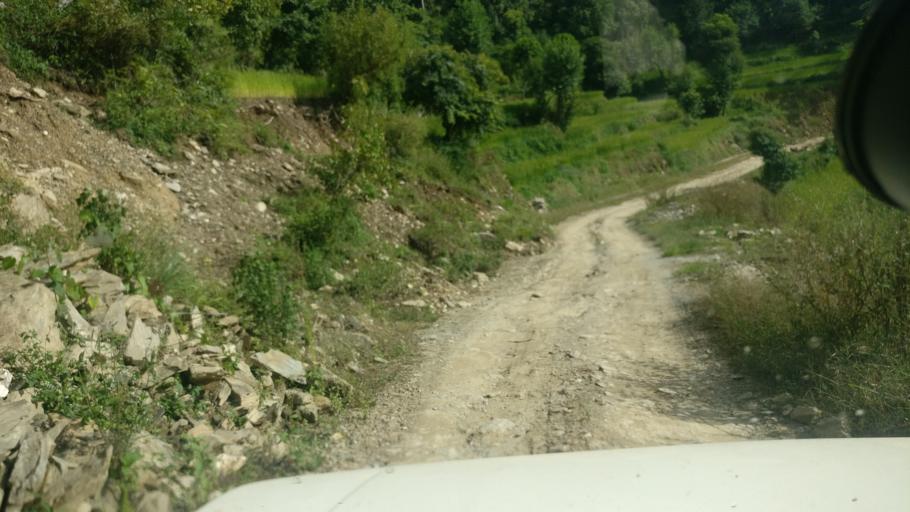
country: NP
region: Western Region
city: Baglung
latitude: 28.2703
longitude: 83.6489
